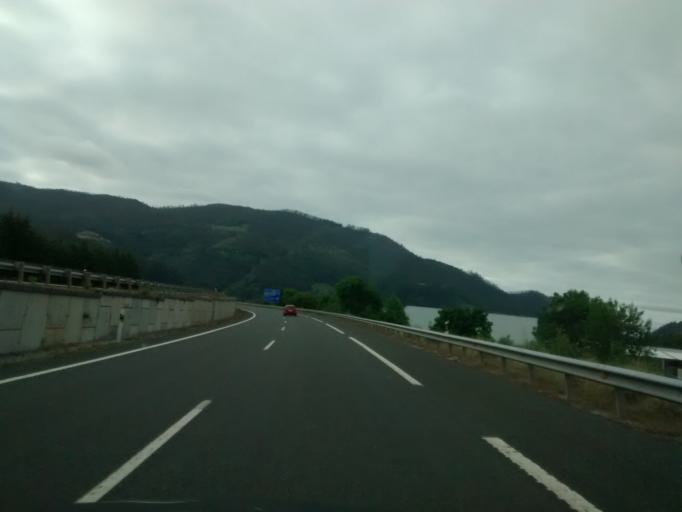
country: ES
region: Cantabria
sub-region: Provincia de Cantabria
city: Los Corrales de Buelna
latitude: 43.2730
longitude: -4.0752
